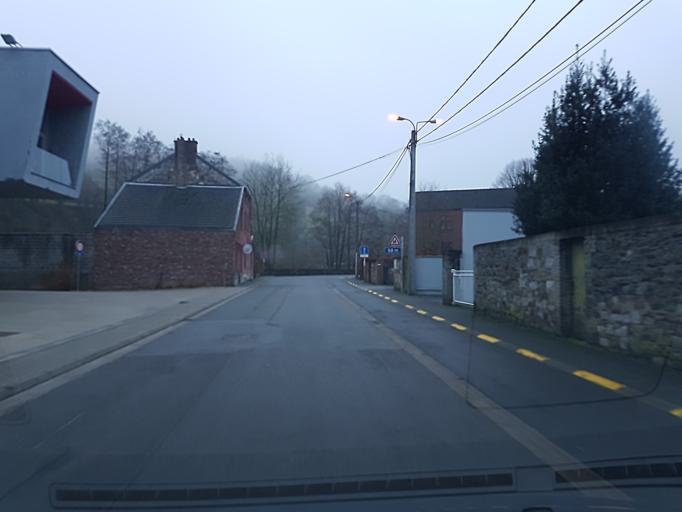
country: BE
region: Wallonia
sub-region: Province de Liege
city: Theux
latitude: 50.5340
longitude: 5.8157
